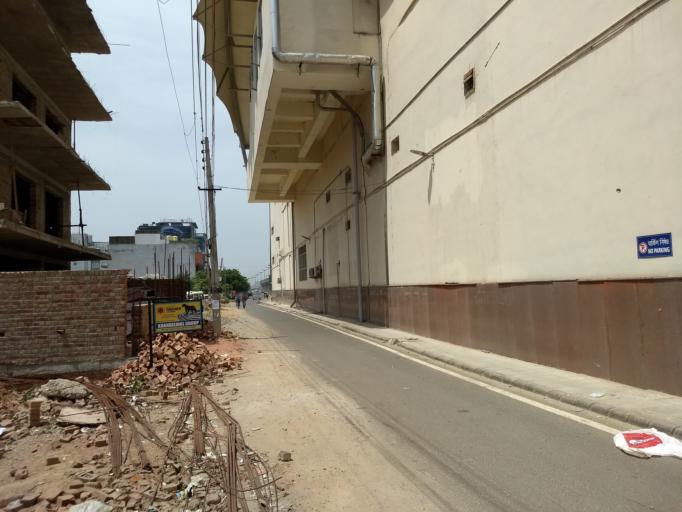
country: IN
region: Haryana
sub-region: Gurgaon
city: Gurgaon
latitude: 28.4571
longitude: 77.0967
